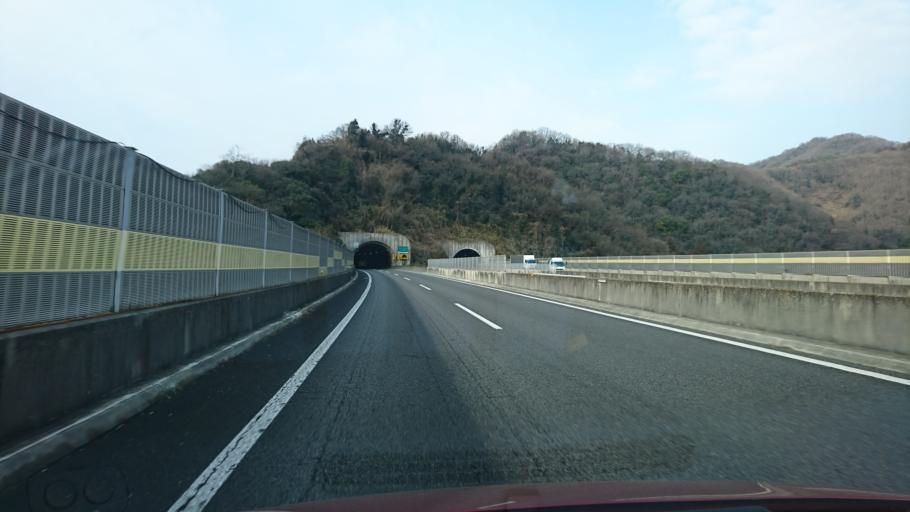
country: JP
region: Okayama
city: Okayama-shi
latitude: 34.7729
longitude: 134.0953
